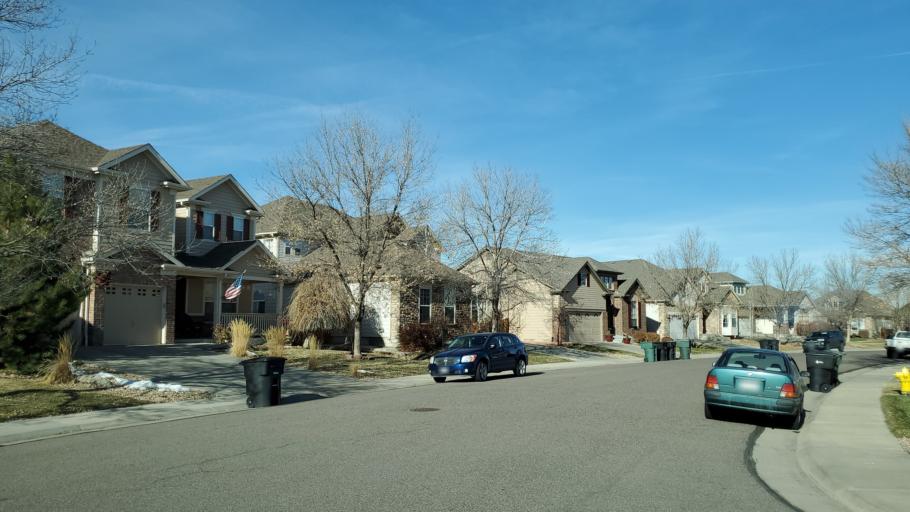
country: US
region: Colorado
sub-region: Adams County
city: Northglenn
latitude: 39.9186
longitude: -104.9481
